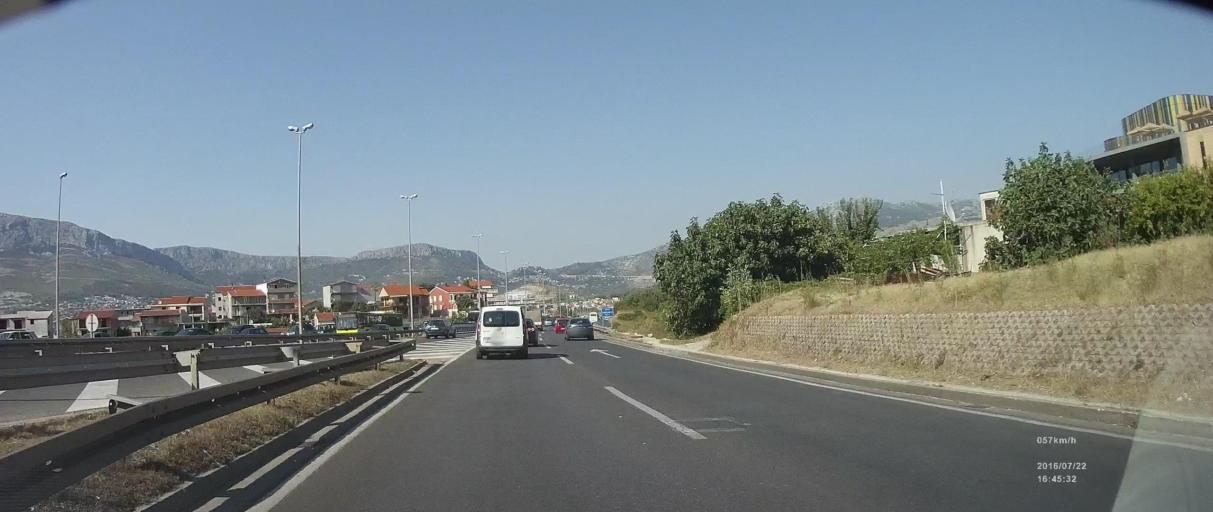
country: HR
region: Splitsko-Dalmatinska
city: Vranjic
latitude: 43.5198
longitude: 16.4822
